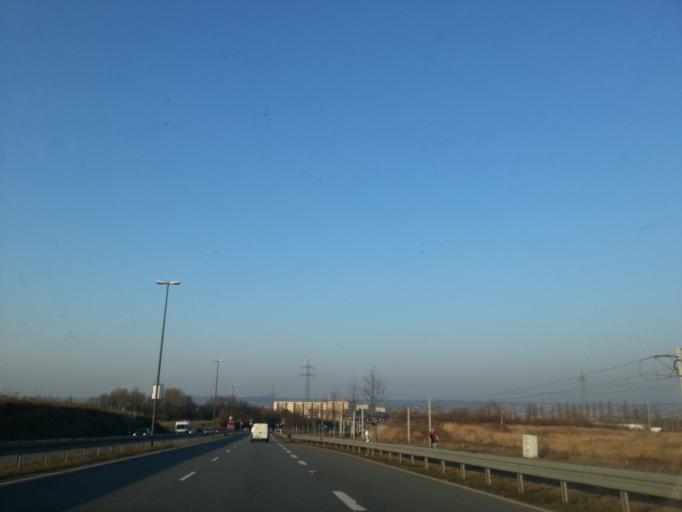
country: DE
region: Saxony
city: Freital
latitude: 51.0429
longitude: 13.6490
